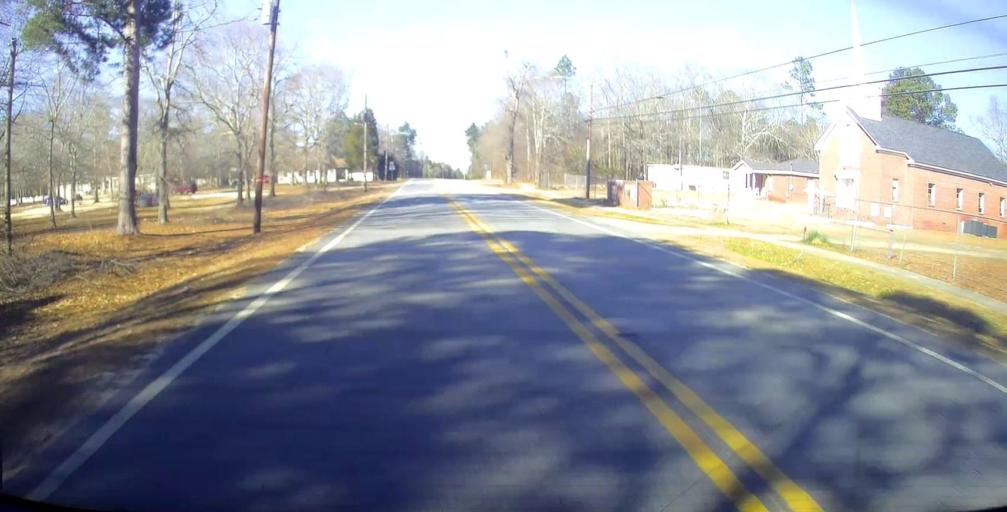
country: US
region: Georgia
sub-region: Taylor County
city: Butler
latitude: 32.5598
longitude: -84.2247
